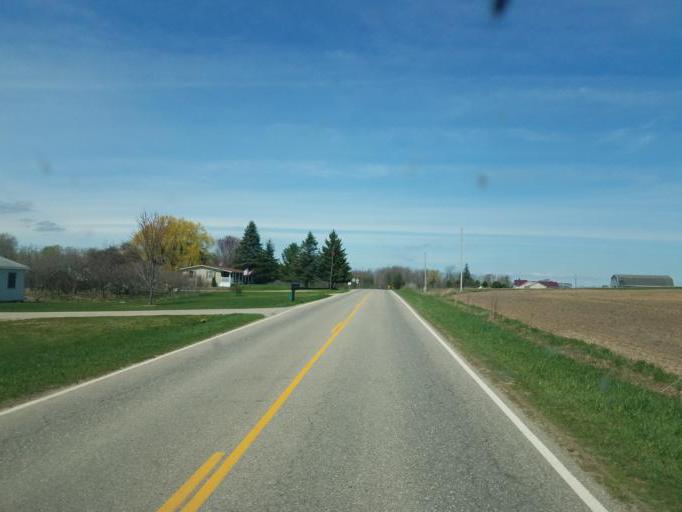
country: US
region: Michigan
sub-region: Clare County
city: Clare
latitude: 43.8232
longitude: -84.6667
